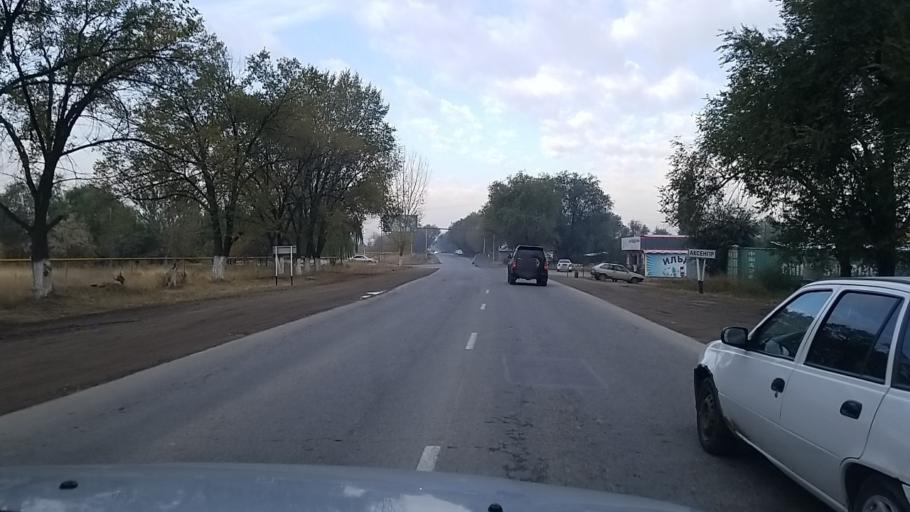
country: KZ
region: Almaty Oblysy
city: Burunday
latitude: 43.3590
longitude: 76.7666
